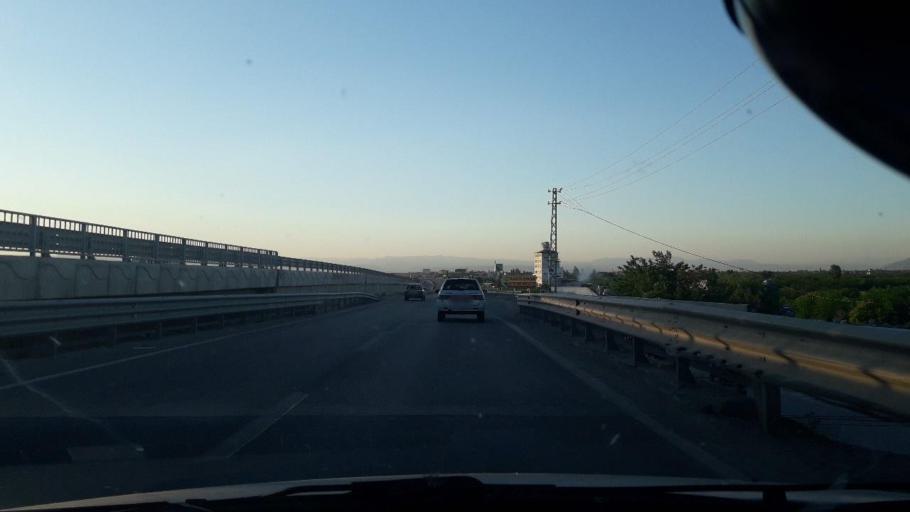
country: TR
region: Malatya
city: Yesilyurt
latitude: 38.3405
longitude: 38.2344
